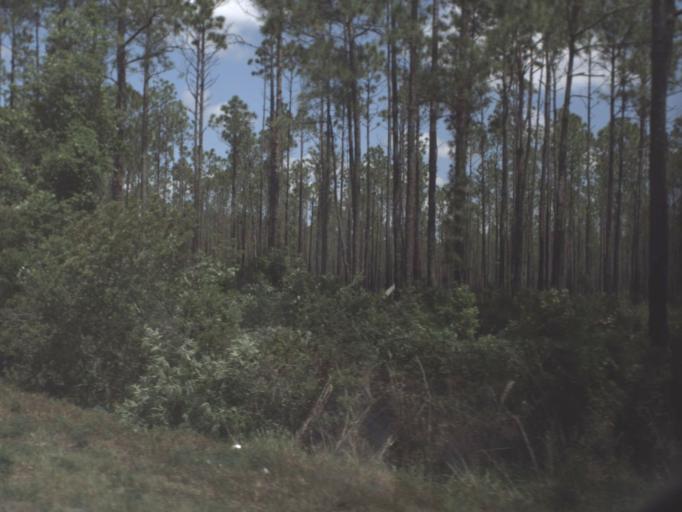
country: US
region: Florida
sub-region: Marion County
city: Silver Springs Shores
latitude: 29.2118
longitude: -81.9507
